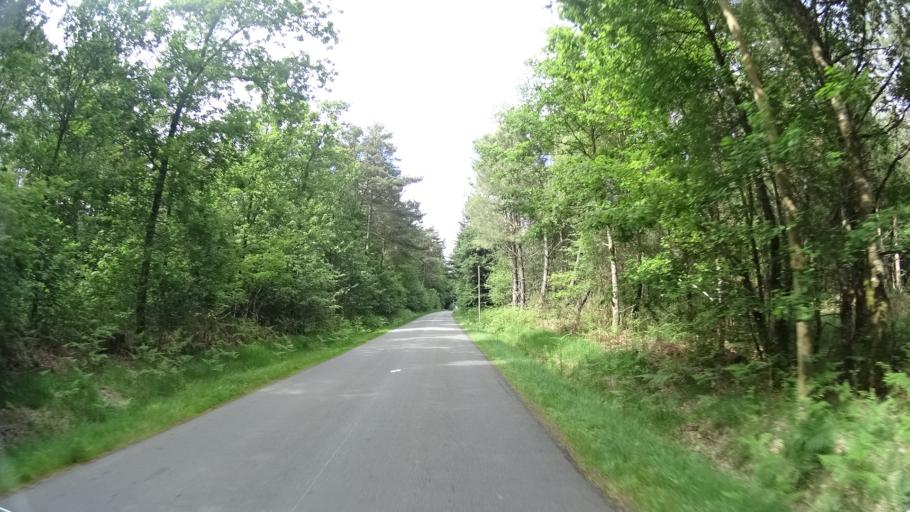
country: FR
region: Brittany
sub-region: Departement d'Ille-et-Vilaine
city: Plelan-le-Grand
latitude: 48.0504
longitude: -2.1048
